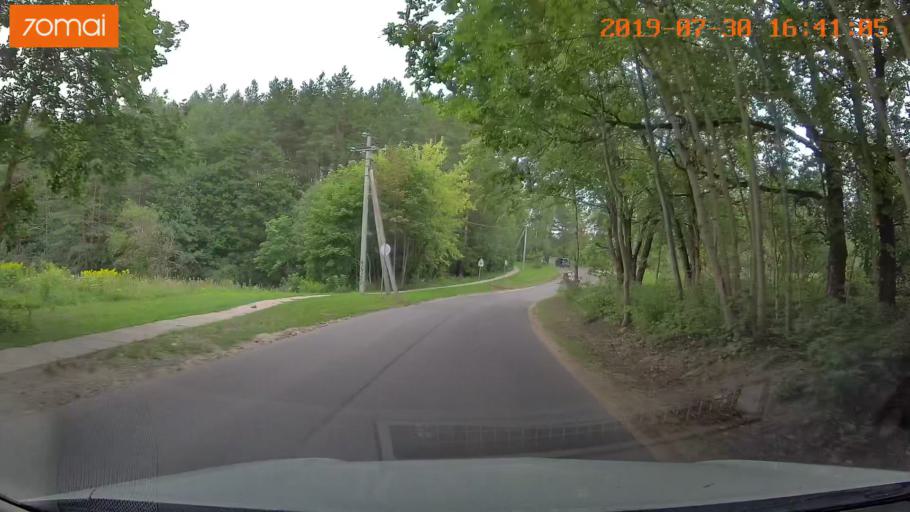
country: LT
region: Vilnius County
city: Rasos
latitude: 54.7088
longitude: 25.3580
